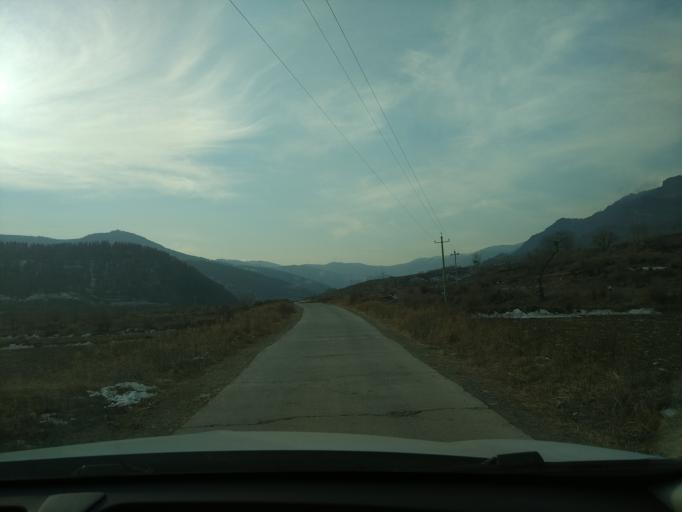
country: CN
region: Hebei
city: Xiwanzi
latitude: 40.8223
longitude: 115.4925
